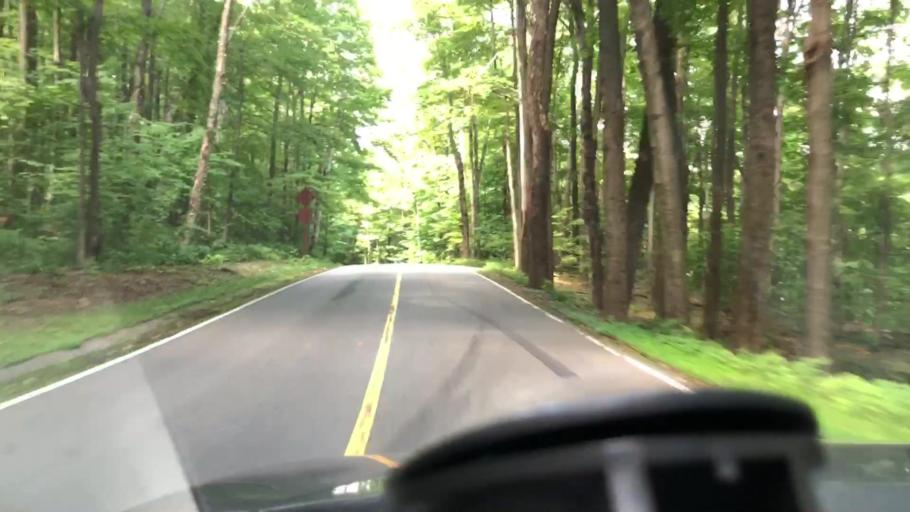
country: US
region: Massachusetts
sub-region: Berkshire County
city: North Adams
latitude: 42.6738
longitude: -73.1492
